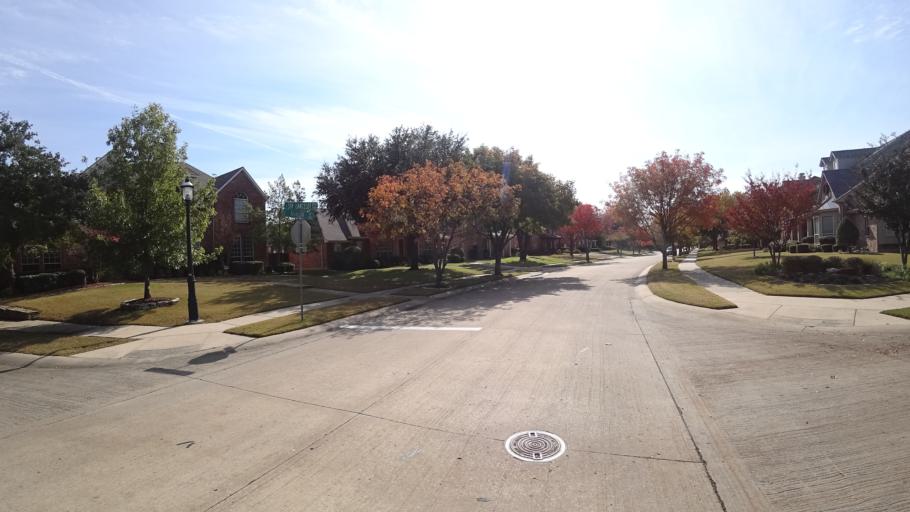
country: US
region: Texas
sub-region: Denton County
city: The Colony
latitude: 33.0359
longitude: -96.8906
